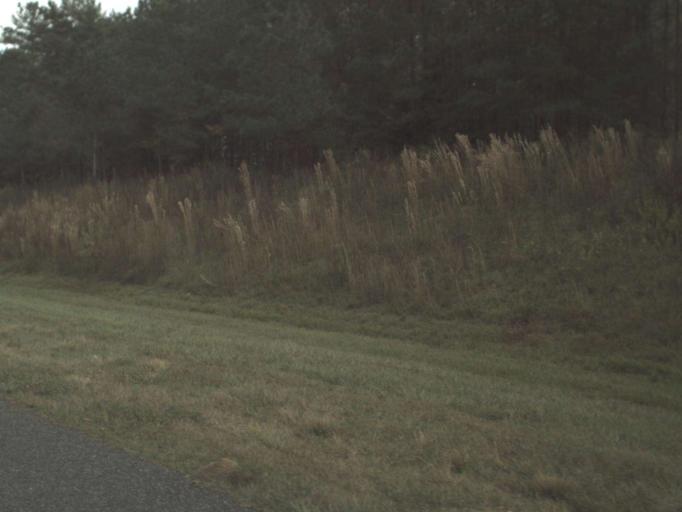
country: US
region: Florida
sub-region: Leon County
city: Tallahassee
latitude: 30.5821
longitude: -84.1981
